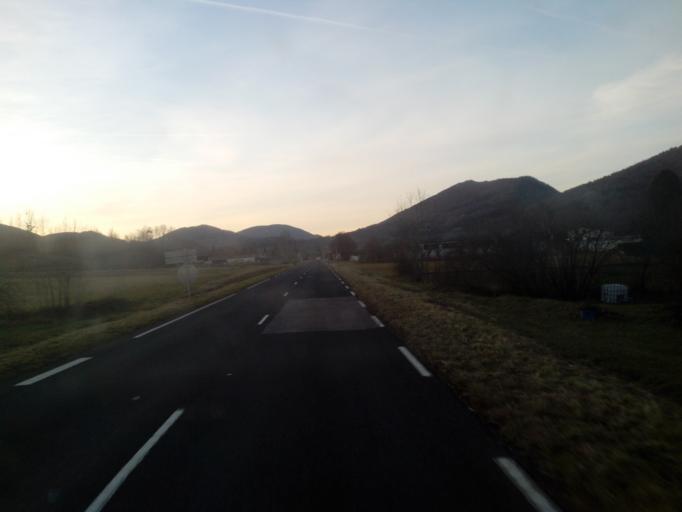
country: FR
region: Midi-Pyrenees
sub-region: Departement de l'Ariege
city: Belesta
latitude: 42.9130
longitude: 1.9156
